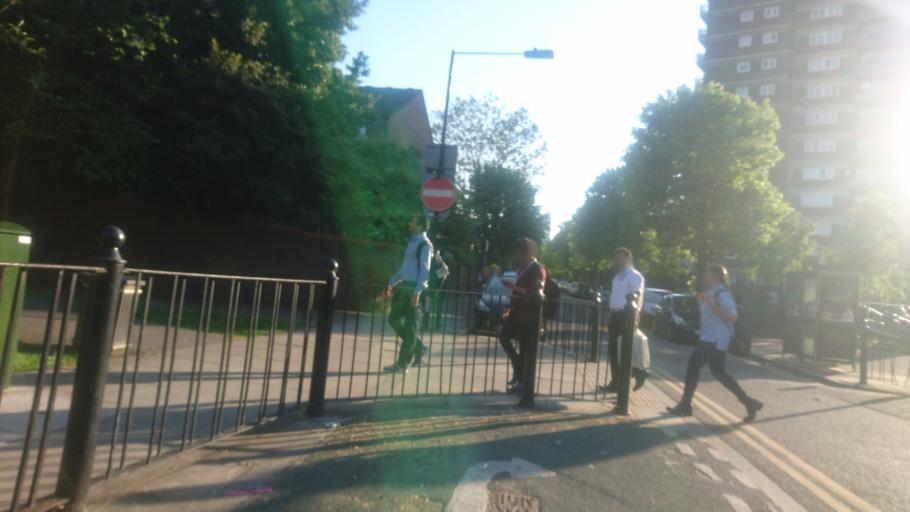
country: GB
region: England
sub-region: Greater London
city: Bethnal Green
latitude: 51.5196
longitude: -0.0635
